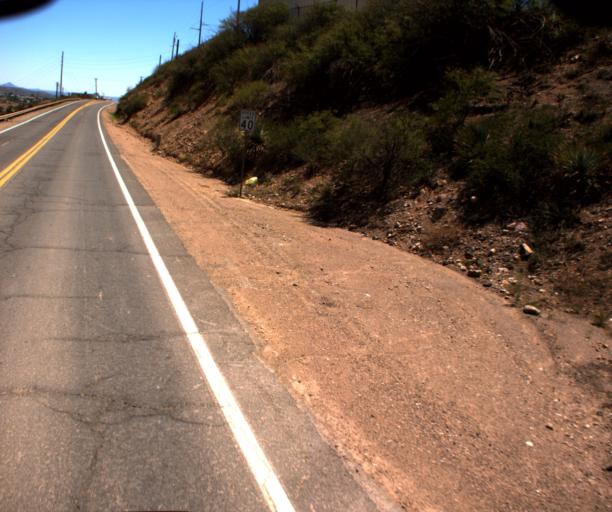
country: US
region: Arizona
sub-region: Greenlee County
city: Clifton
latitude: 33.0590
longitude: -109.3305
